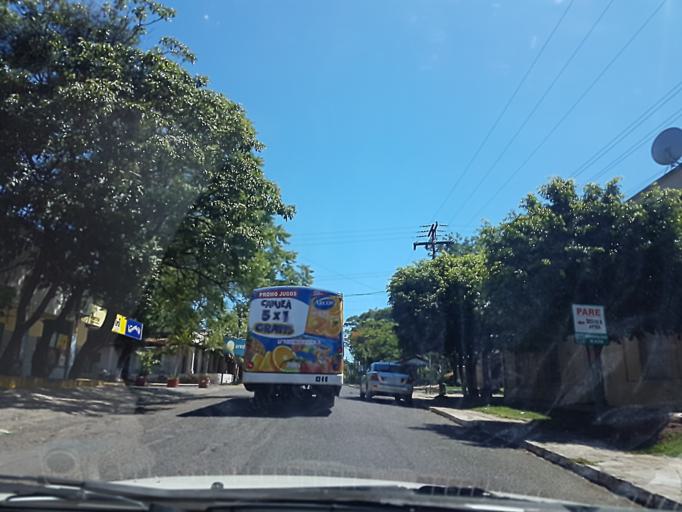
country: PY
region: Cordillera
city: Altos
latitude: -25.2606
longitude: -57.2490
